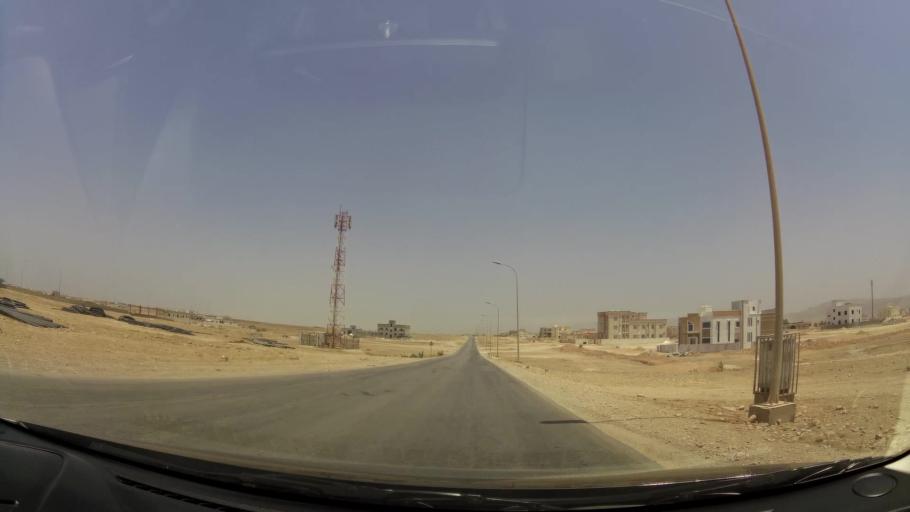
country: OM
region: Zufar
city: Salalah
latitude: 17.0916
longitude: 54.1866
